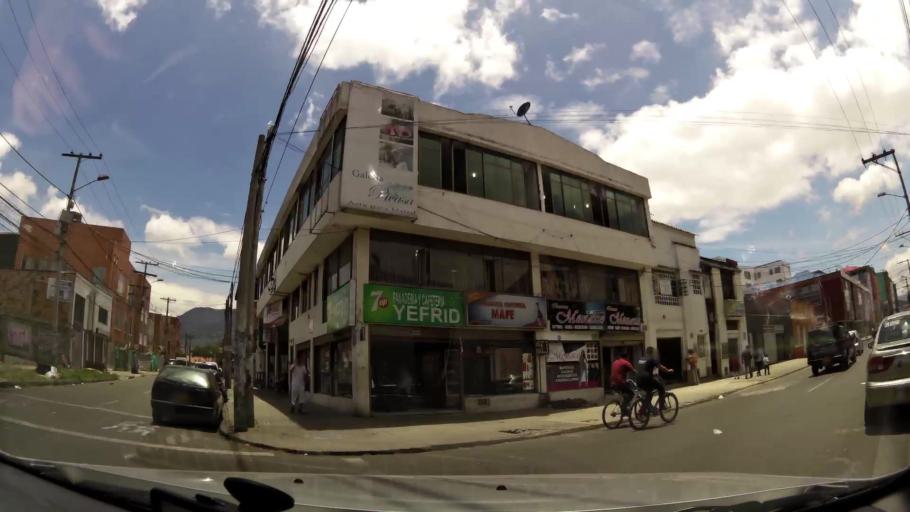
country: CO
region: Bogota D.C.
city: Bogota
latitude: 4.5853
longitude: -74.0985
